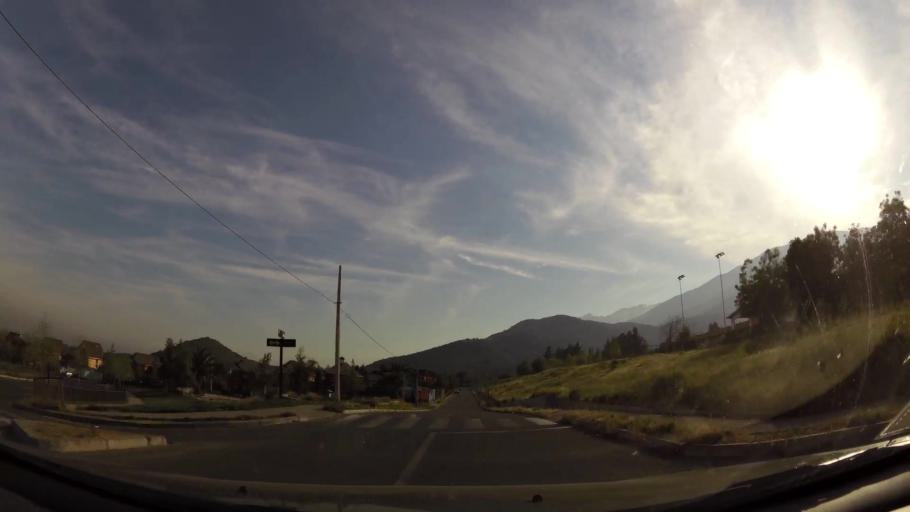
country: CL
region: Santiago Metropolitan
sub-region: Provincia de Cordillera
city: Puente Alto
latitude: -33.5634
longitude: -70.5436
